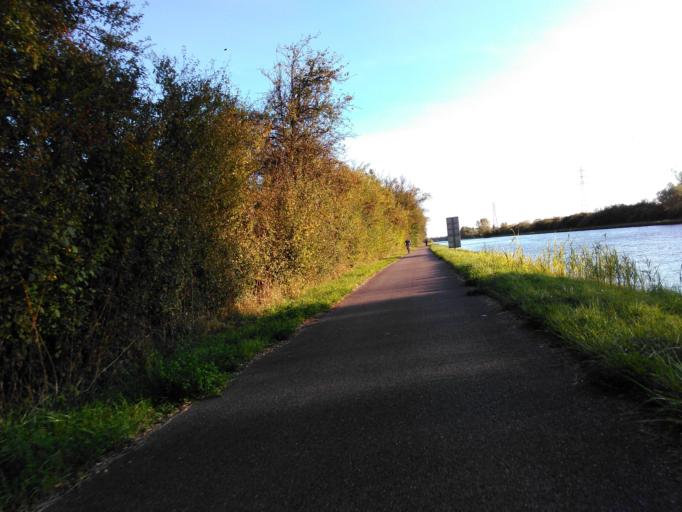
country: FR
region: Lorraine
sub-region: Departement de la Moselle
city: Talange
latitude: 49.2162
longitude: 6.1823
